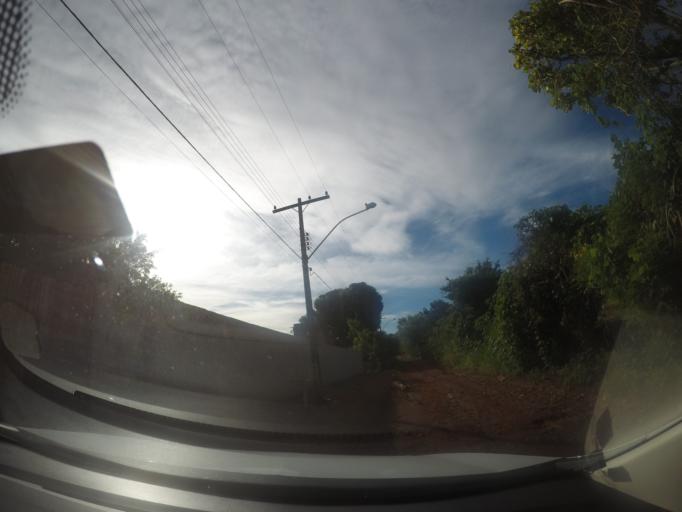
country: BR
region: Goias
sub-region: Goiania
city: Goiania
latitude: -16.6400
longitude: -49.3514
